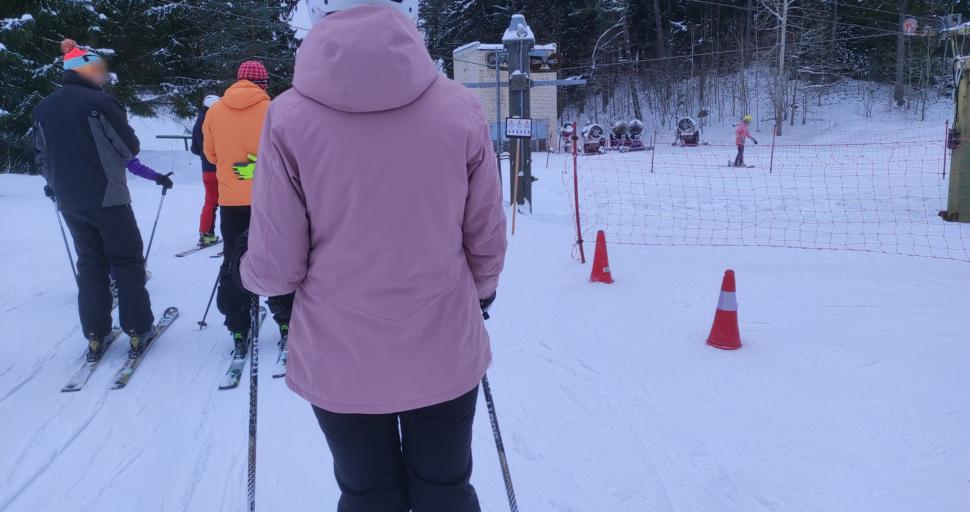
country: LV
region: Plavinu
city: Plavinas
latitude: 56.6599
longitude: 25.7144
